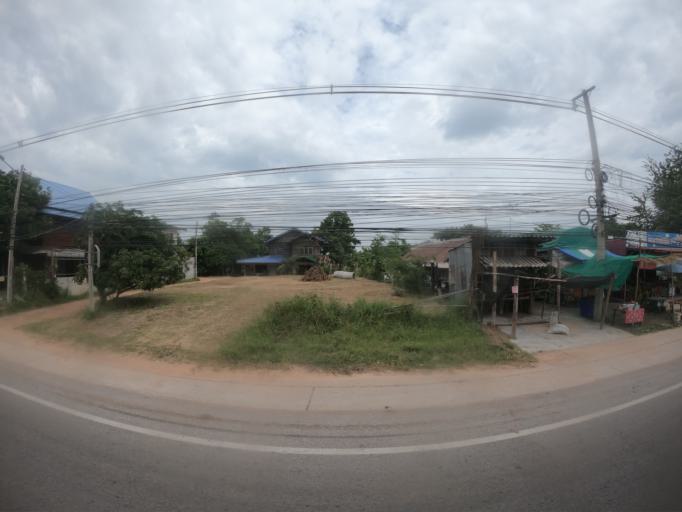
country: TH
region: Maha Sarakham
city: Maha Sarakham
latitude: 16.1675
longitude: 103.3273
